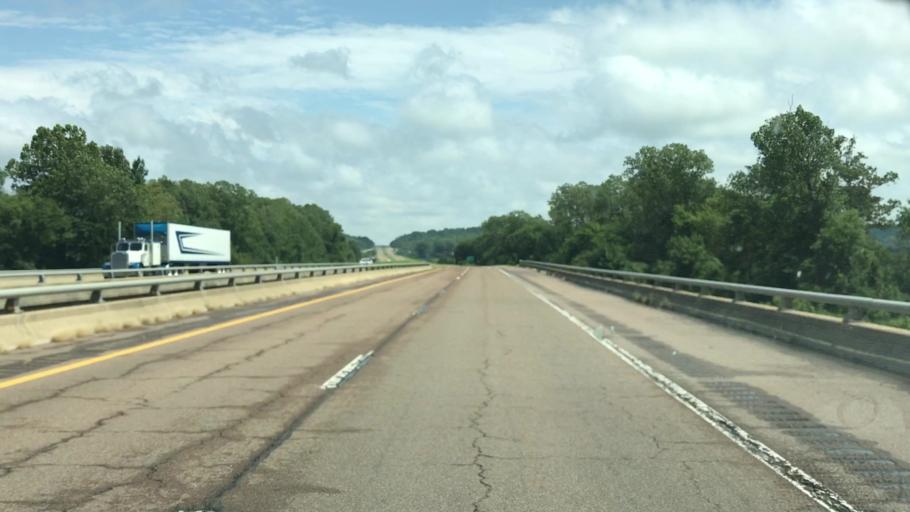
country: US
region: Tennessee
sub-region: Dyer County
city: Dyersburg
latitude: 36.0783
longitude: -89.5184
